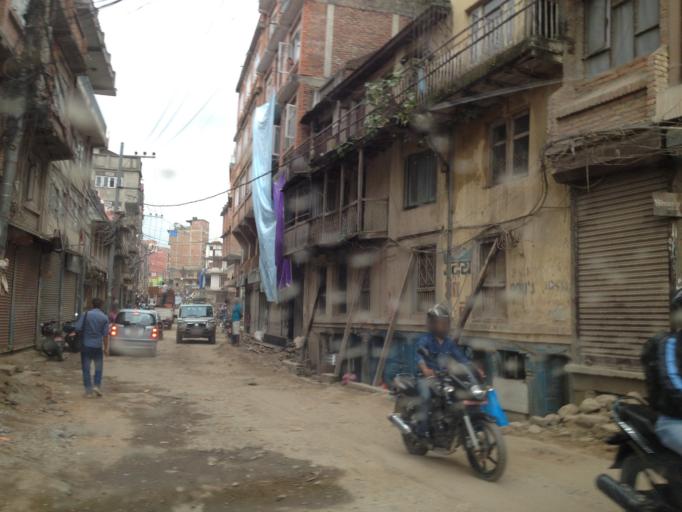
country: NP
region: Central Region
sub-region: Bagmati Zone
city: Kathmandu
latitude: 27.7017
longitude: 85.3017
